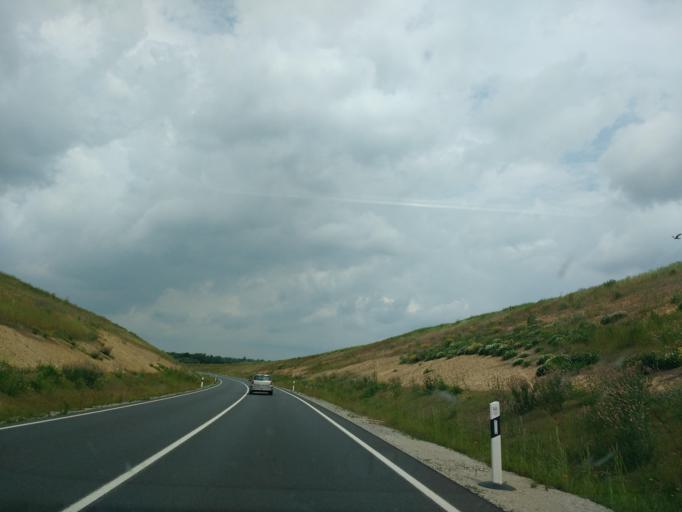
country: DE
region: Saxony-Anhalt
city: Theissen
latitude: 51.0842
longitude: 12.1204
